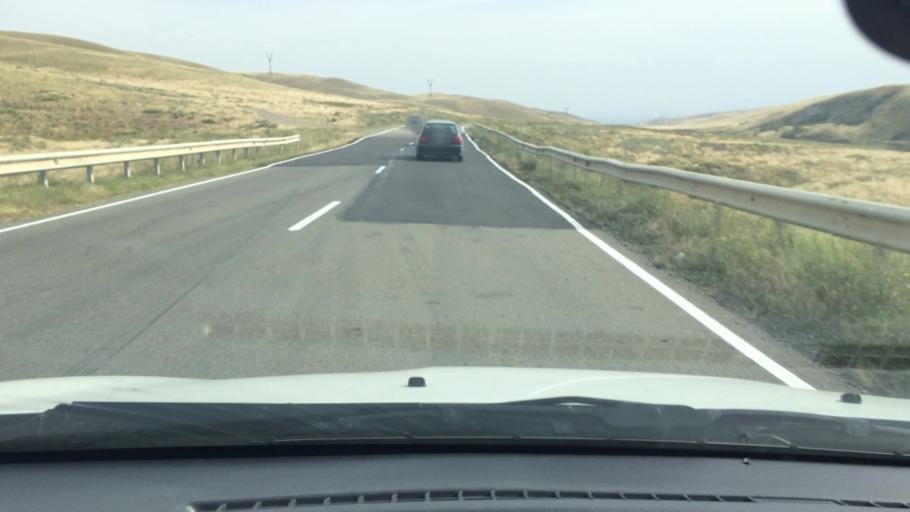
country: GE
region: Kvemo Kartli
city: Rust'avi
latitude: 41.5201
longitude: 44.9398
